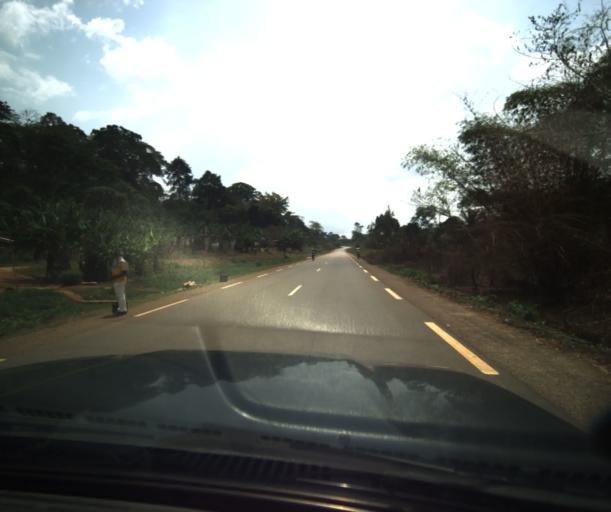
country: CM
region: Centre
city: Akono
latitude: 3.6180
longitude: 11.3176
